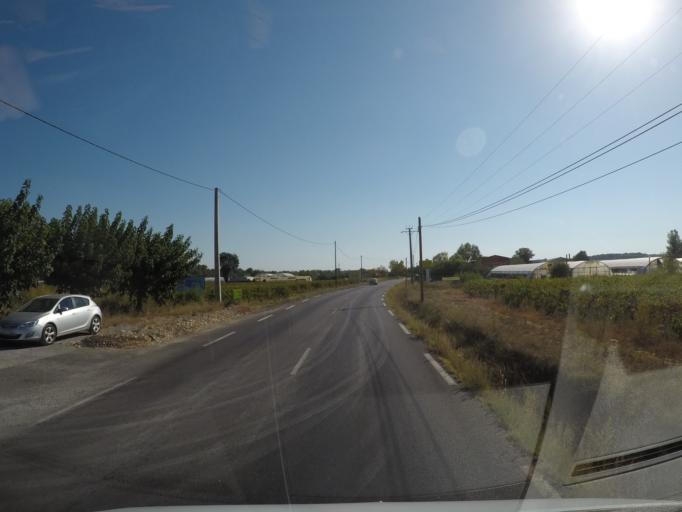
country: FR
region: Languedoc-Roussillon
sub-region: Departement du Gard
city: Lezan
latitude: 44.0246
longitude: 4.0322
